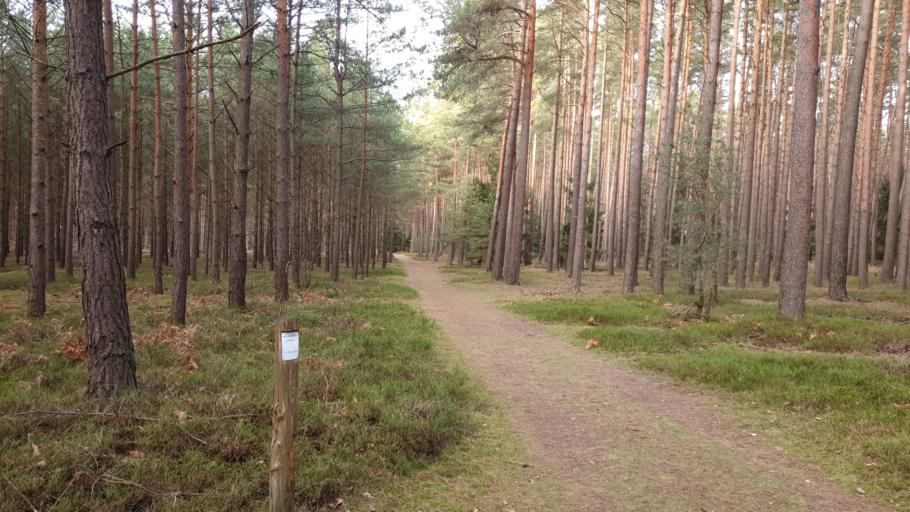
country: DE
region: Mecklenburg-Vorpommern
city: Wesenberg
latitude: 53.3077
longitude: 12.9323
